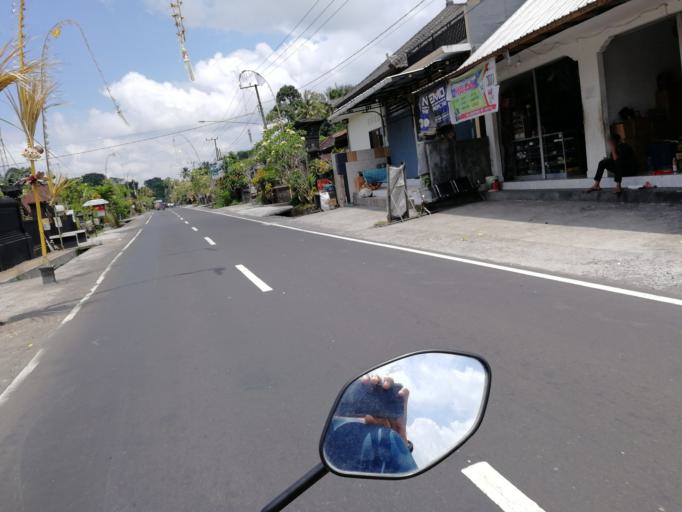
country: ID
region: Bali
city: Banjar Kubu
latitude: -8.4285
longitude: 115.4257
